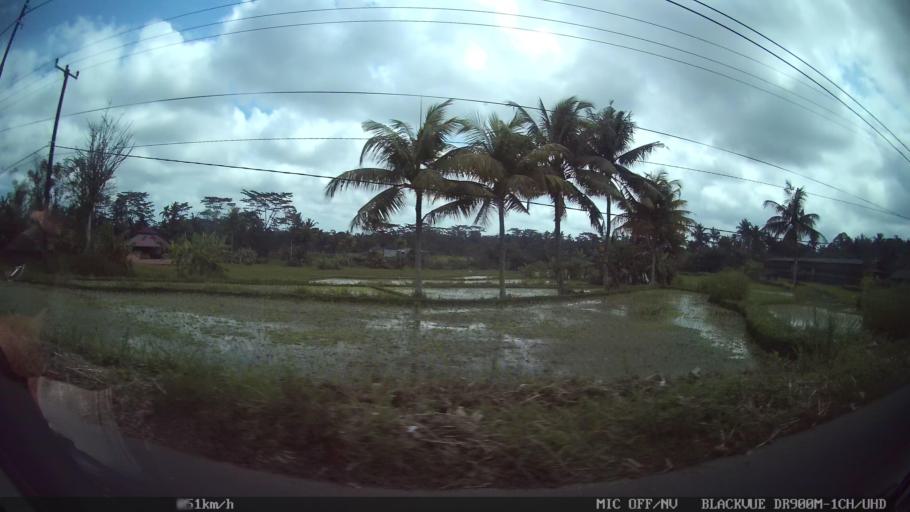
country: ID
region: Bali
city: Banjar Madangan Kaja
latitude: -8.4842
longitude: 115.3213
